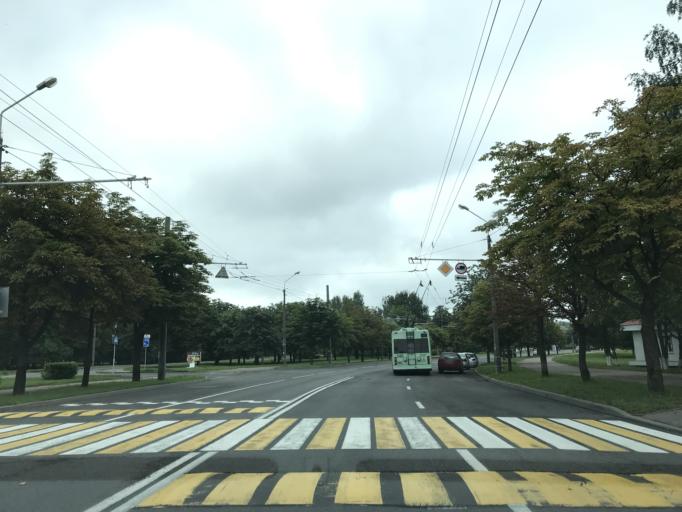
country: BY
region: Minsk
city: Borovlyany
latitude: 53.9496
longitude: 27.6404
